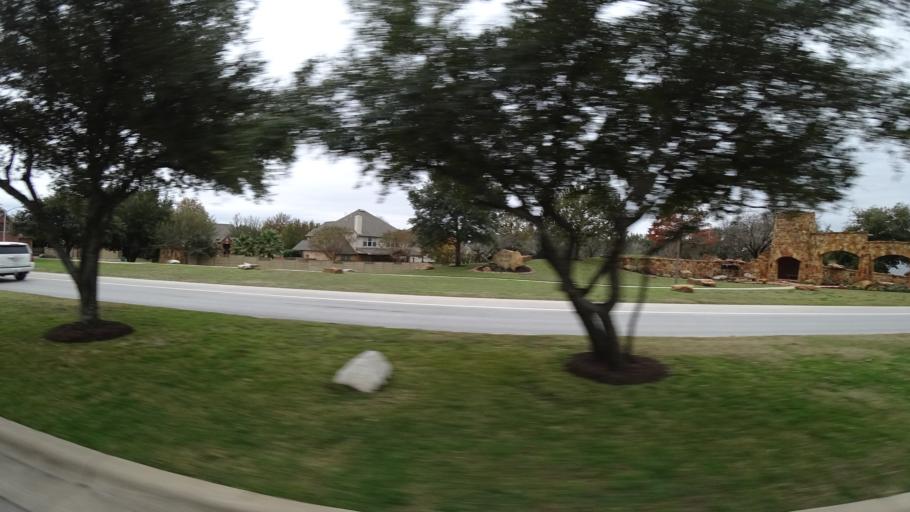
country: US
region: Texas
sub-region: Williamson County
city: Cedar Park
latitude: 30.4731
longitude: -97.8504
